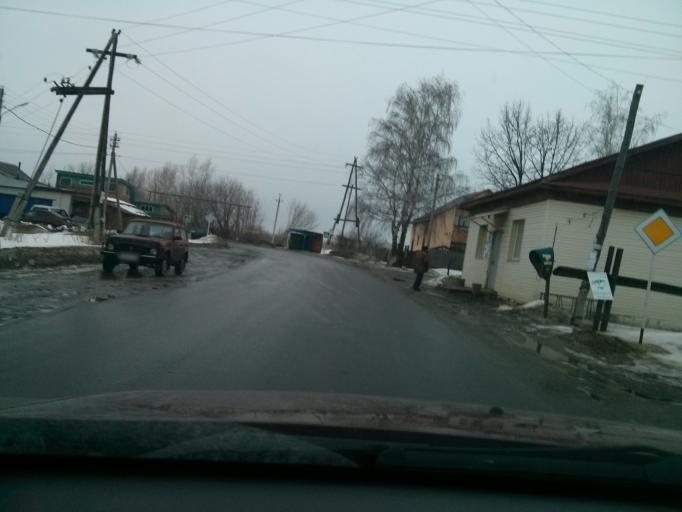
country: RU
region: Vladimir
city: Murom
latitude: 55.5461
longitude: 42.0261
